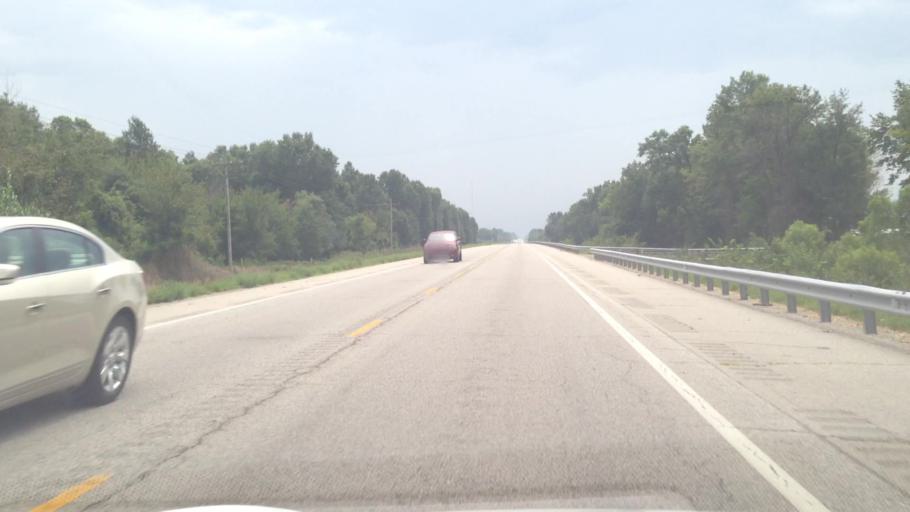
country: US
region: Kansas
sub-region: Cherokee County
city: Galena
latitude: 37.1417
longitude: -94.7044
